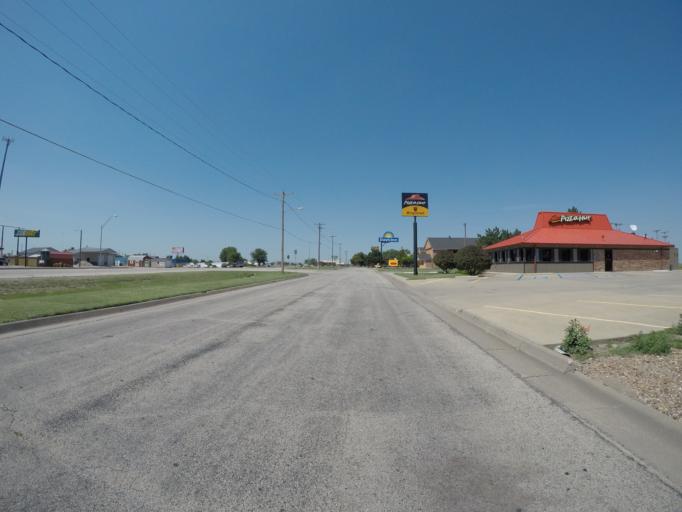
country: US
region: Kansas
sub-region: Russell County
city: Russell
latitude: 38.8667
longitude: -98.8540
